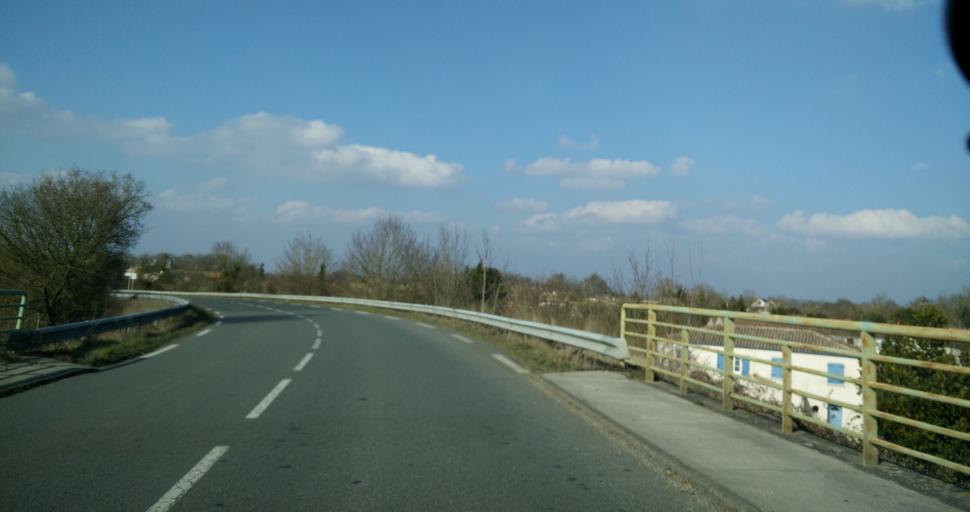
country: FR
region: Poitou-Charentes
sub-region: Departement des Deux-Sevres
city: Mauze-sur-le-Mignon
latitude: 46.1879
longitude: -0.6739
